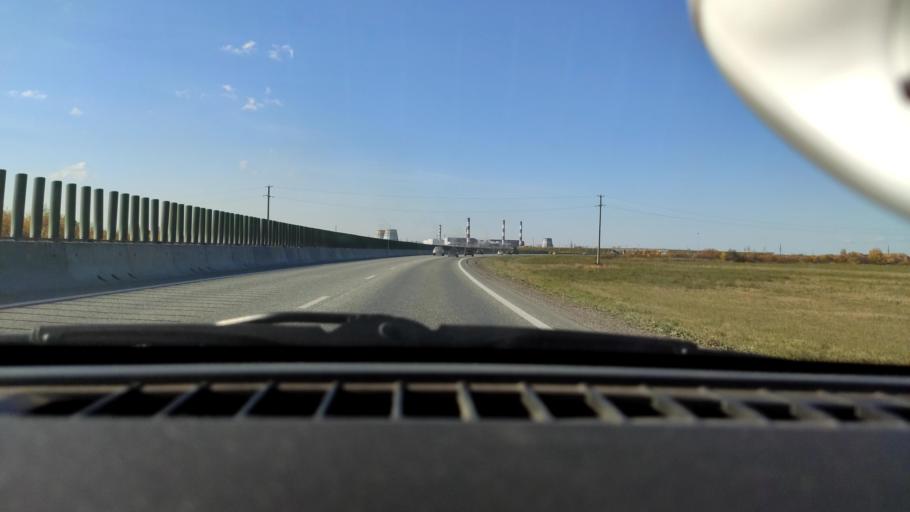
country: RU
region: Perm
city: Froly
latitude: 57.9286
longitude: 56.1907
